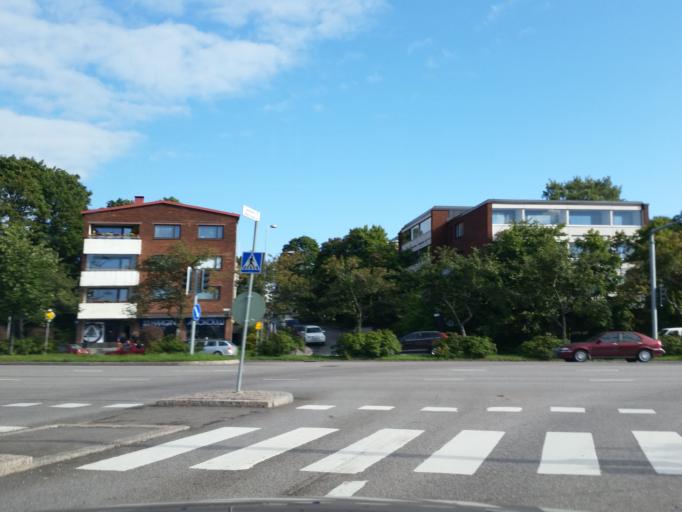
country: FI
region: Uusimaa
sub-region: Helsinki
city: Teekkarikylae
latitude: 60.2089
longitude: 24.8898
